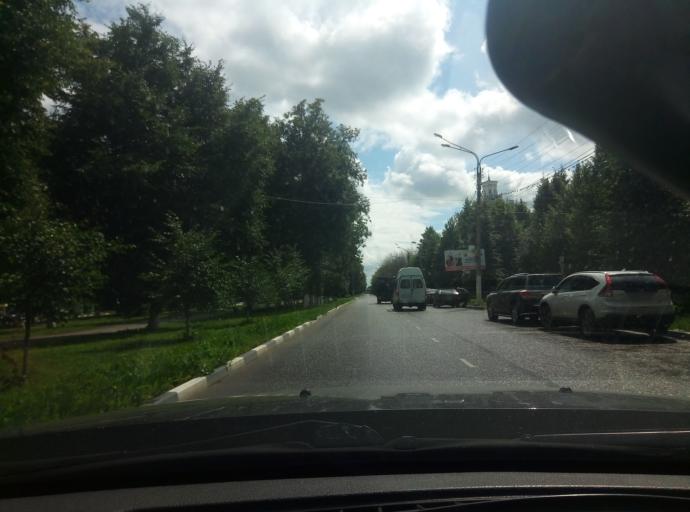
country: RU
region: Tula
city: Novomoskovsk
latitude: 54.0122
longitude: 38.2961
